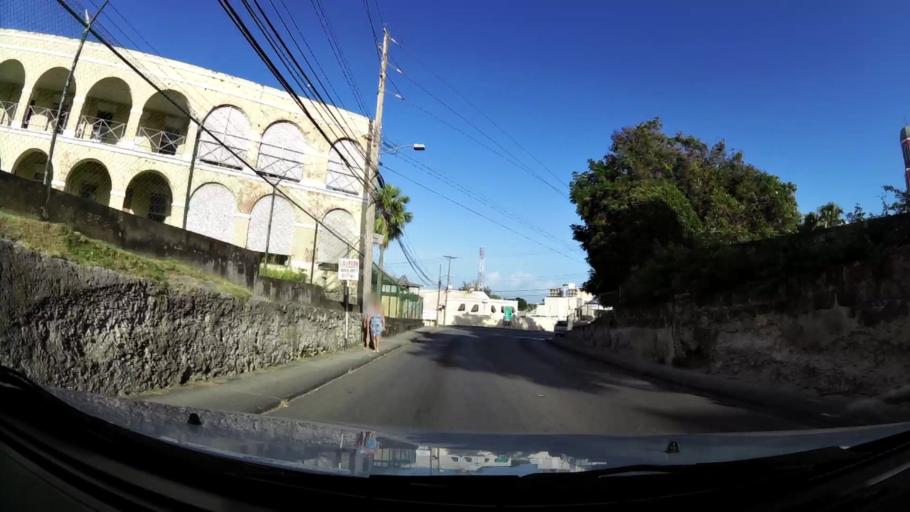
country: BB
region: Saint Michael
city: Bridgetown
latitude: 13.0798
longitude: -59.6071
